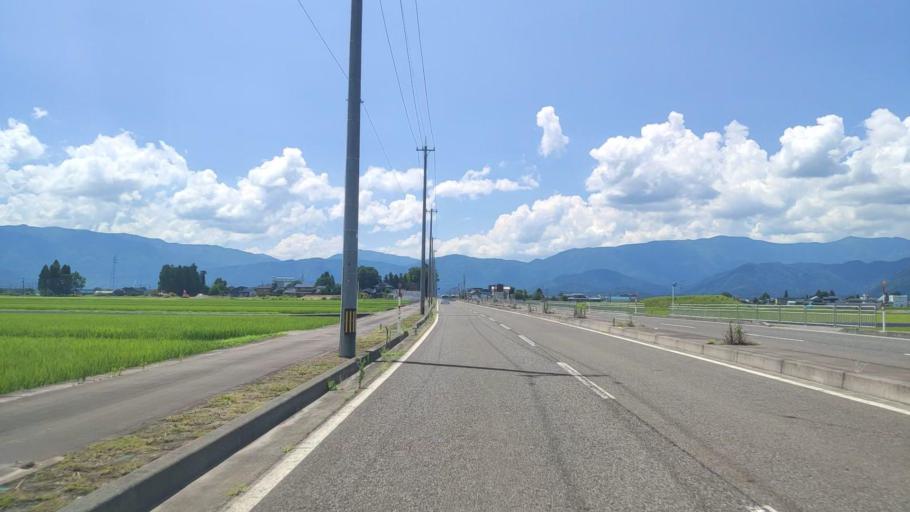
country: JP
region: Fukui
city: Ono
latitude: 36.0005
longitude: 136.5089
